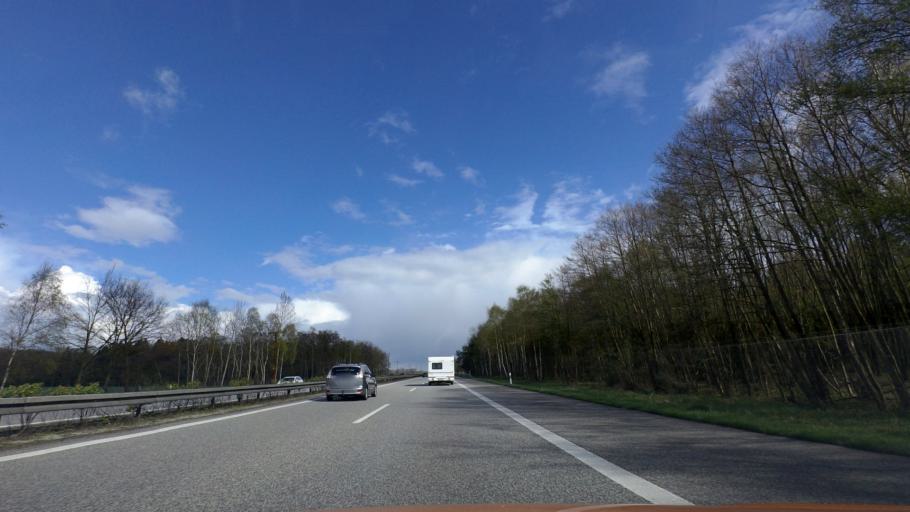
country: DE
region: Mecklenburg-Vorpommern
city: Wittenburg
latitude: 53.5061
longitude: 11.0088
